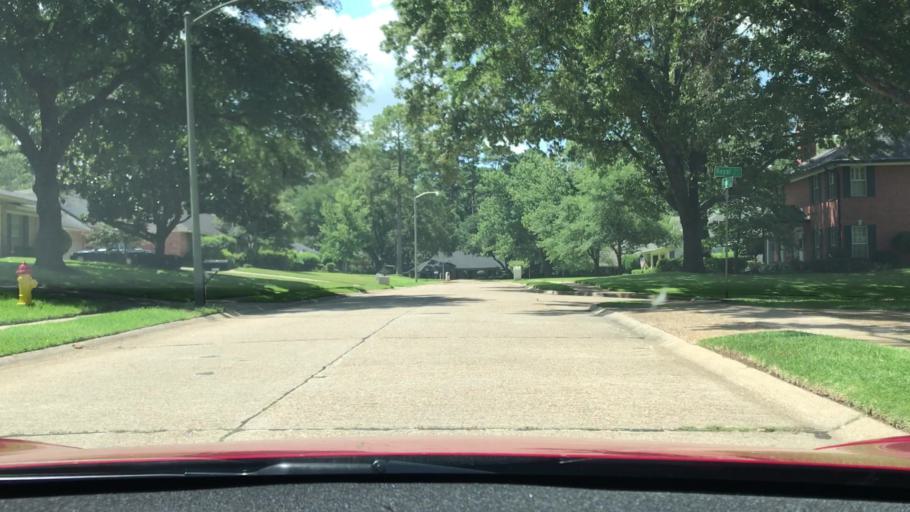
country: US
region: Louisiana
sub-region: Bossier Parish
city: Bossier City
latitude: 32.4281
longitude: -93.7297
